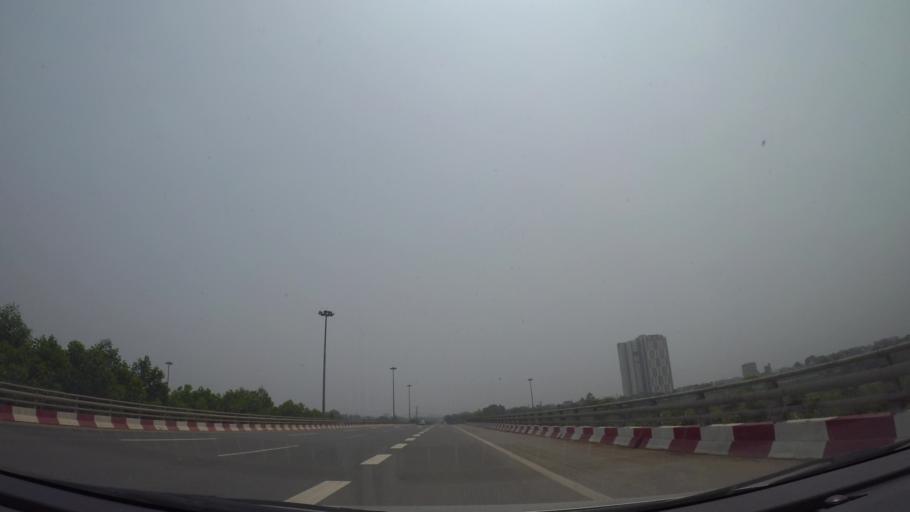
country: VN
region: Ha Noi
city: Lien Quan
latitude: 20.9900
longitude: 105.5258
